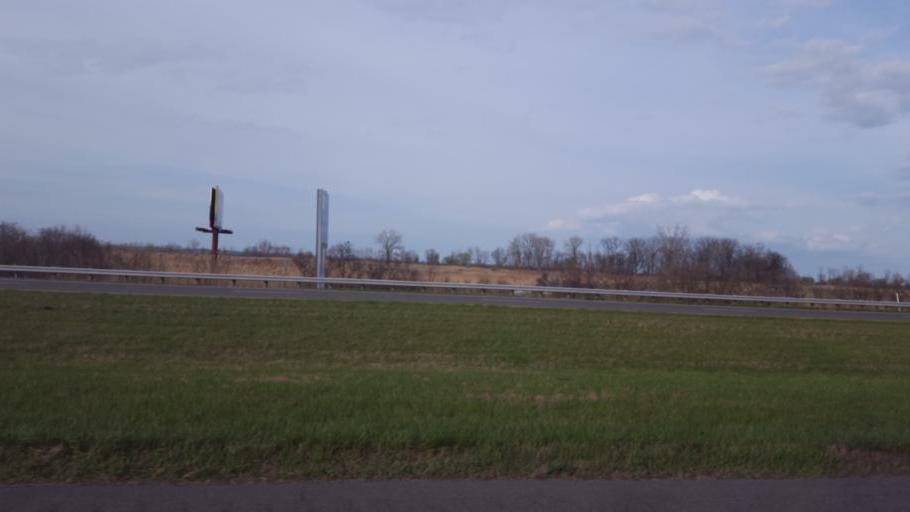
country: US
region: Ohio
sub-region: Erie County
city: Sandusky
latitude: 41.4531
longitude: -82.7993
